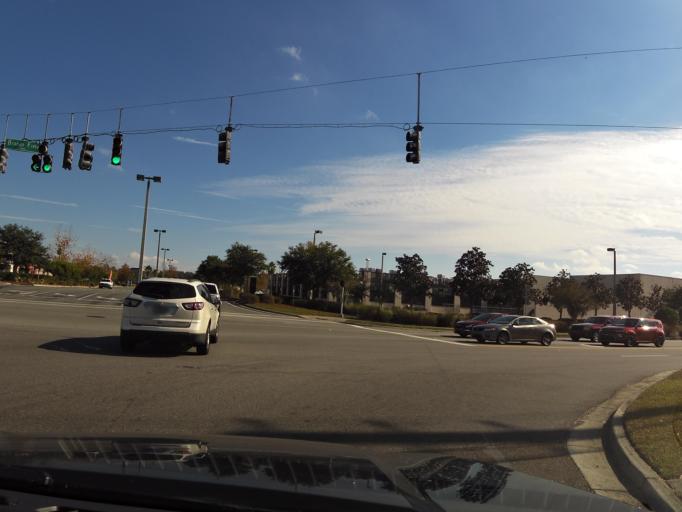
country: US
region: Florida
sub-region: Clay County
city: Middleburg
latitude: 30.1069
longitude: -81.8311
